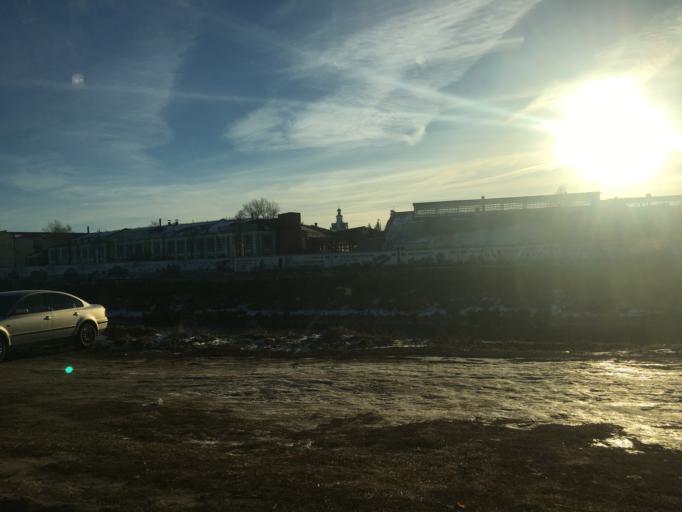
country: RU
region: Tula
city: Tula
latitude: 54.2047
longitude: 37.6117
